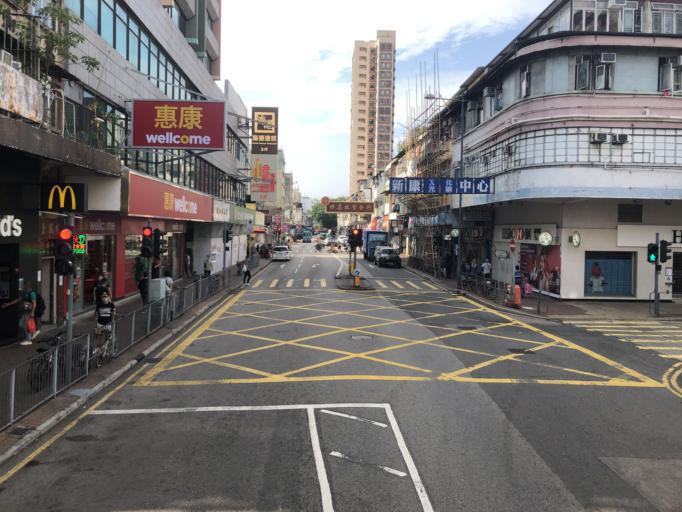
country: HK
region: Tai Po
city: Tai Po
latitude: 22.5040
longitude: 114.1268
